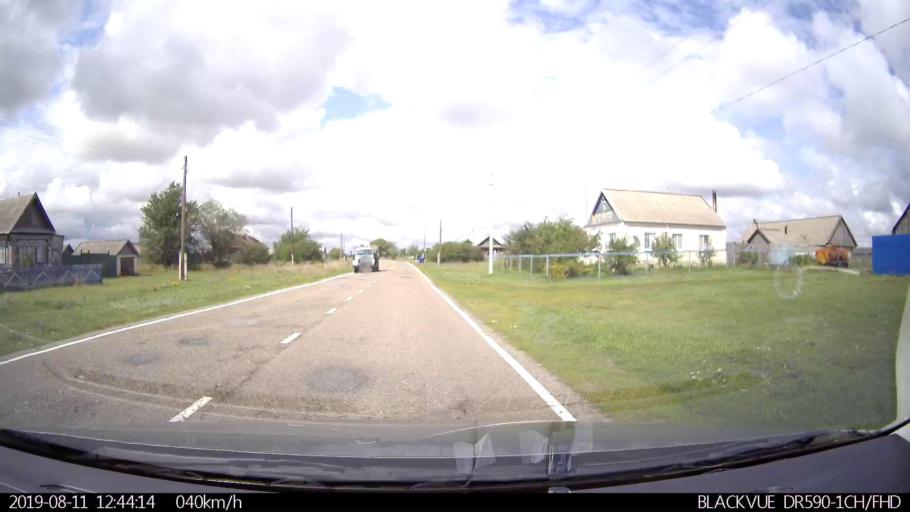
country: RU
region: Ulyanovsk
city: Ignatovka
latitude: 53.8539
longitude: 47.7376
